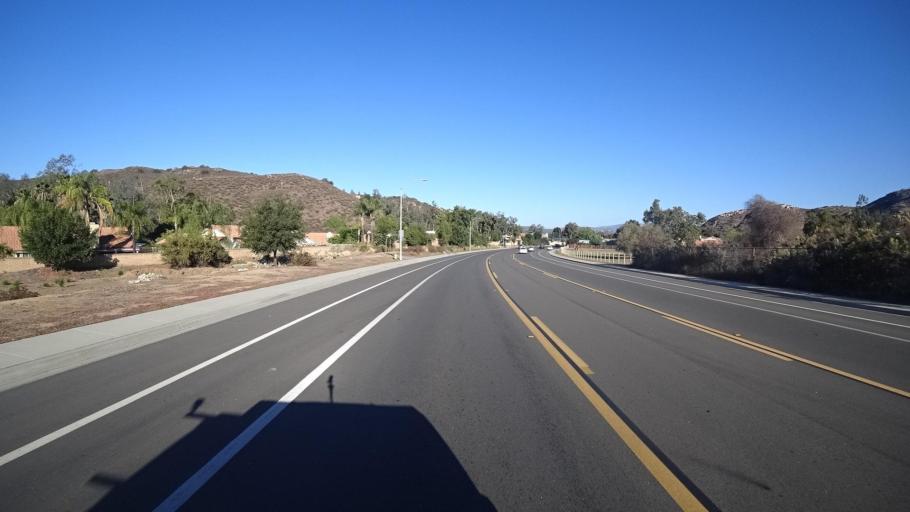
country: US
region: California
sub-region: San Diego County
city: Lakeside
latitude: 32.8411
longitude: -116.9147
